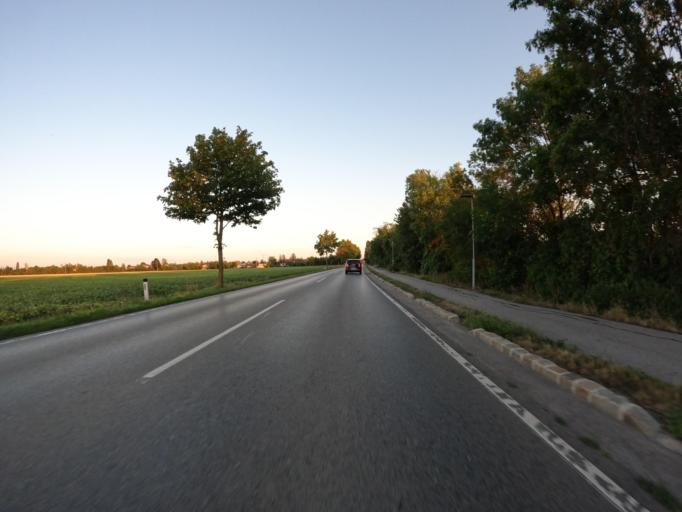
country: AT
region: Lower Austria
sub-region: Politischer Bezirk Baden
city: Pfaffstatten
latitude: 47.9956
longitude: 16.2741
